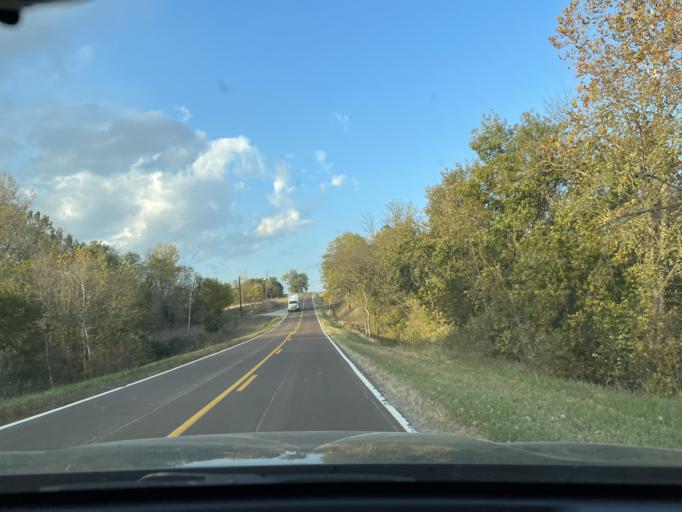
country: US
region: Missouri
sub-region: Andrew County
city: Savannah
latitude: 39.9085
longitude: -94.8785
